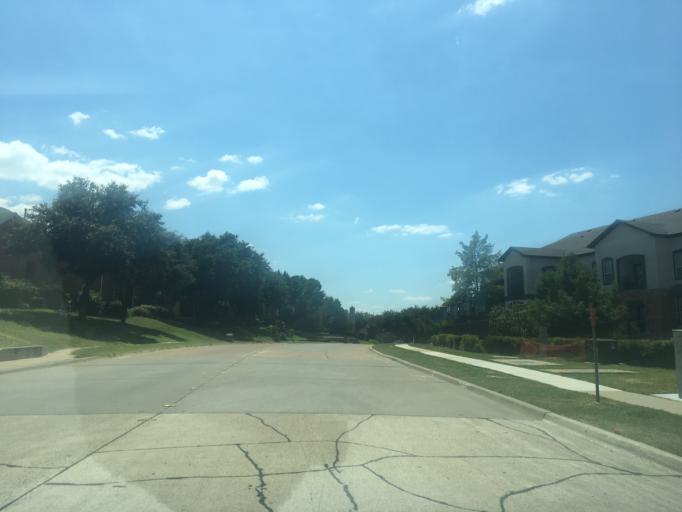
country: US
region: Texas
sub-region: Denton County
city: Lewisville
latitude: 33.0136
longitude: -96.9972
